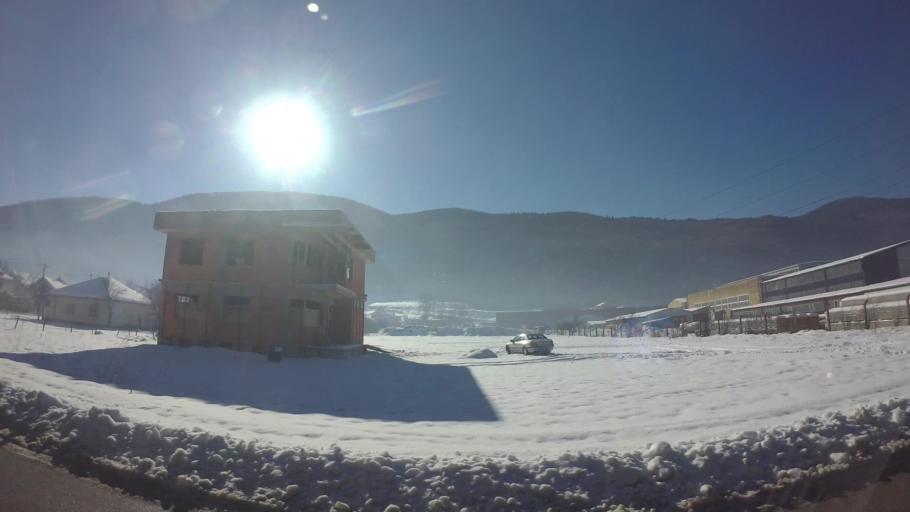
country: BA
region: Federation of Bosnia and Herzegovina
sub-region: Kanton Sarajevo
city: Sarajevo
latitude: 43.7917
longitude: 18.3342
